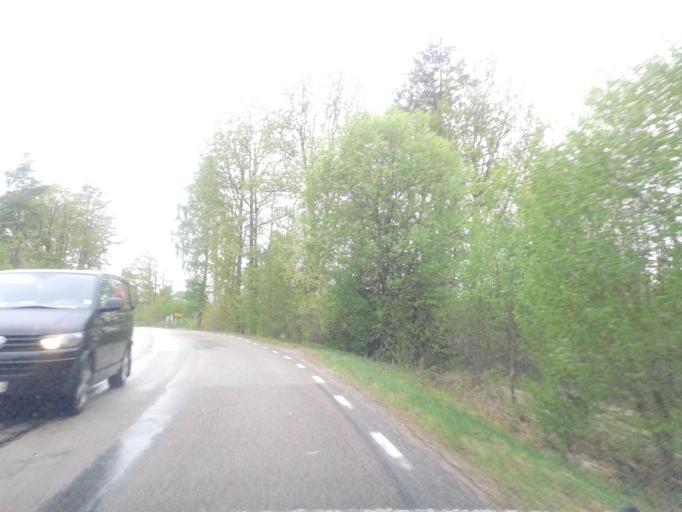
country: SE
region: Vaestra Goetaland
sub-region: Lilla Edets Kommun
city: Lodose
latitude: 58.0802
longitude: 11.9888
